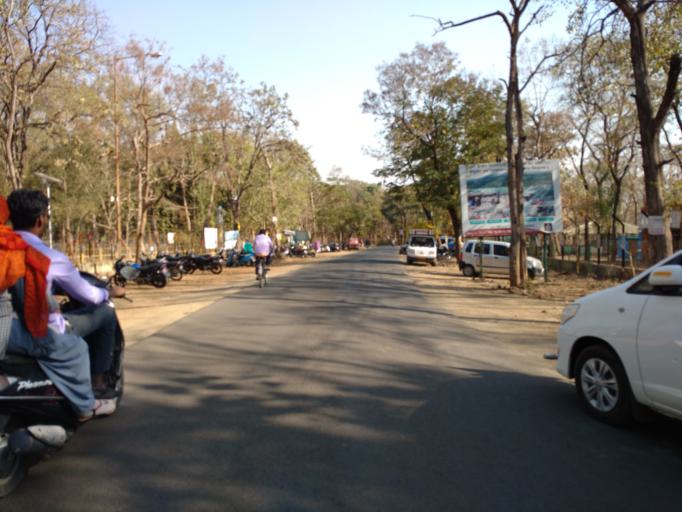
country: IN
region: Maharashtra
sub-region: Nagpur Division
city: Nagpur
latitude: 21.1680
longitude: 79.0637
